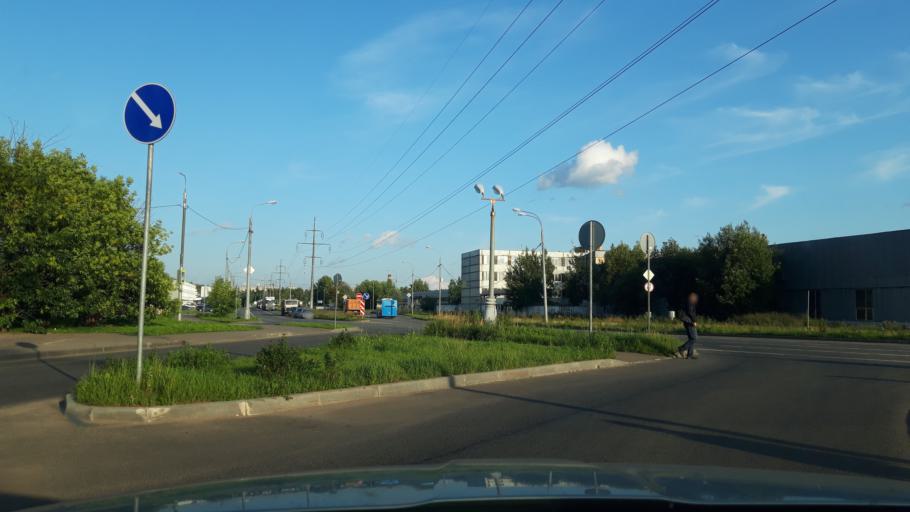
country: RU
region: Moskovskaya
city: Alabushevo
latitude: 56.0116
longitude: 37.1589
